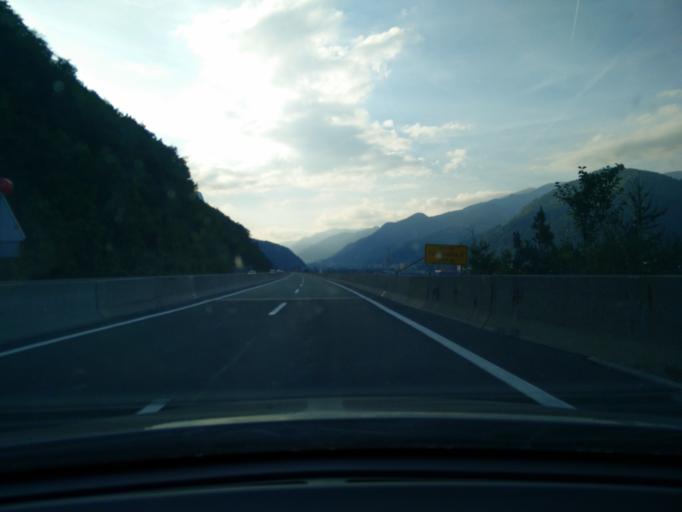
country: SI
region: Jesenice
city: Jesenice
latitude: 46.4249
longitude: 14.0749
